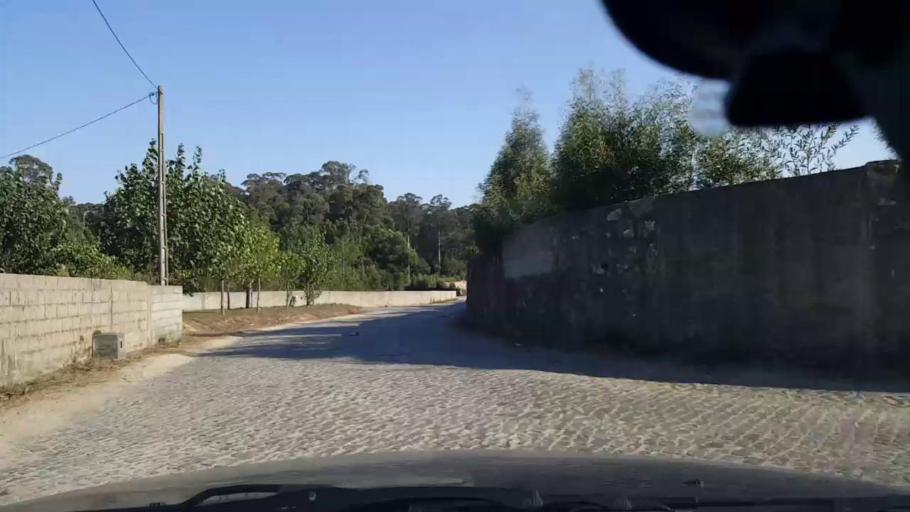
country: PT
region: Porto
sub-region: Vila do Conde
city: Arvore
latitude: 41.3478
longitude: -8.6927
